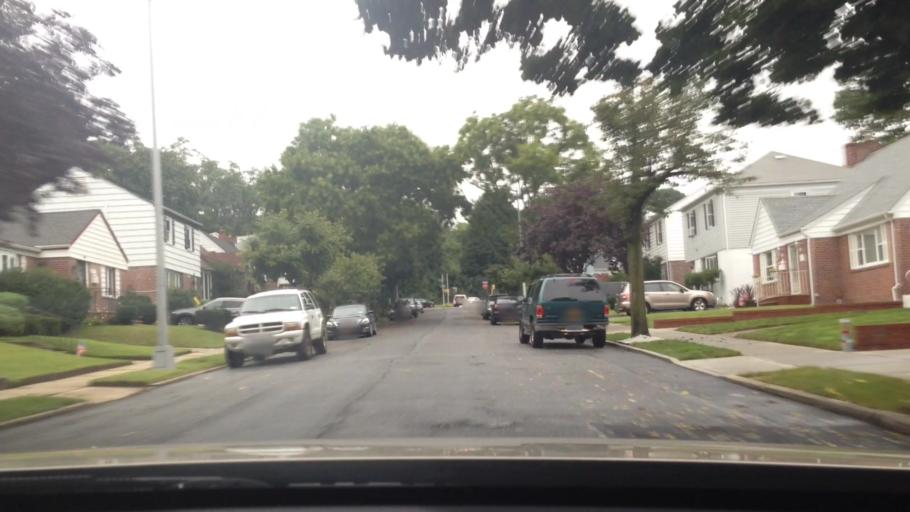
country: US
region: New York
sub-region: Nassau County
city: Bellerose Terrace
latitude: 40.7356
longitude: -73.7399
